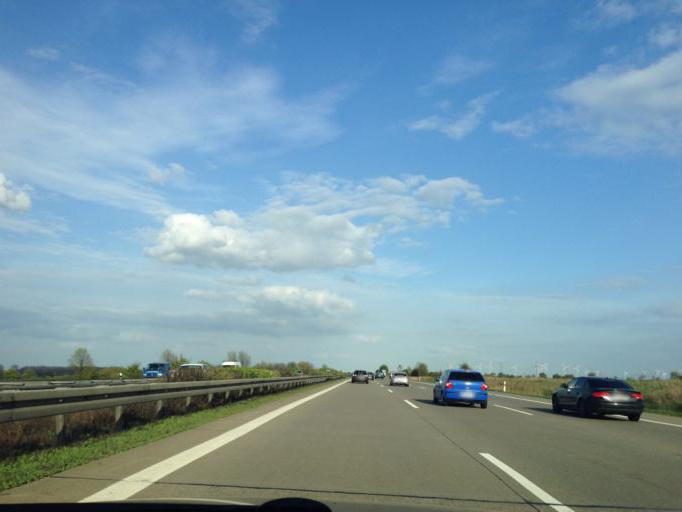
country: DE
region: Saxony-Anhalt
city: Erxleben
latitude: 52.2014
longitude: 11.2122
